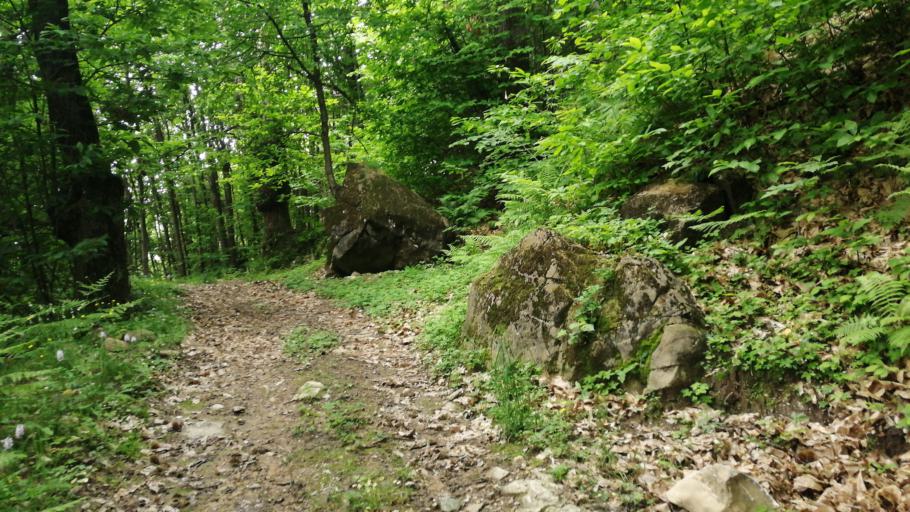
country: IT
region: Piedmont
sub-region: Provincia di Cuneo
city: Montaldo di Mondovi
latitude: 44.3143
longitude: 7.8643
